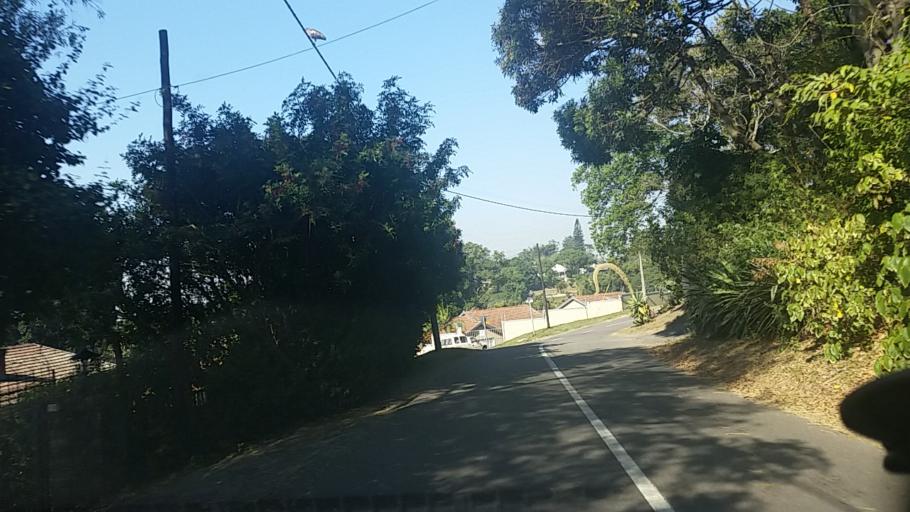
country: ZA
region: KwaZulu-Natal
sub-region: eThekwini Metropolitan Municipality
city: Berea
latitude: -29.8401
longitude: 30.9108
